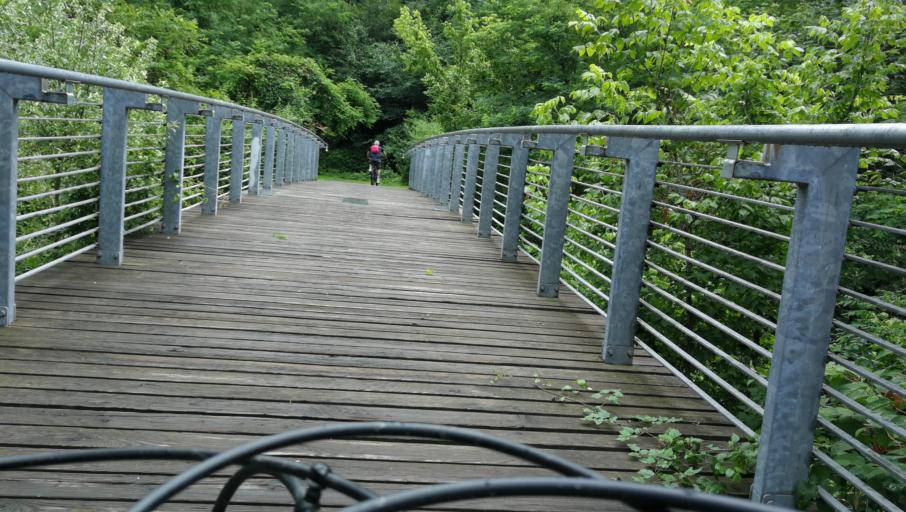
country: IT
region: Lombardy
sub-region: Provincia di Varese
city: Cittiglio
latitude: 45.8932
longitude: 8.6547
